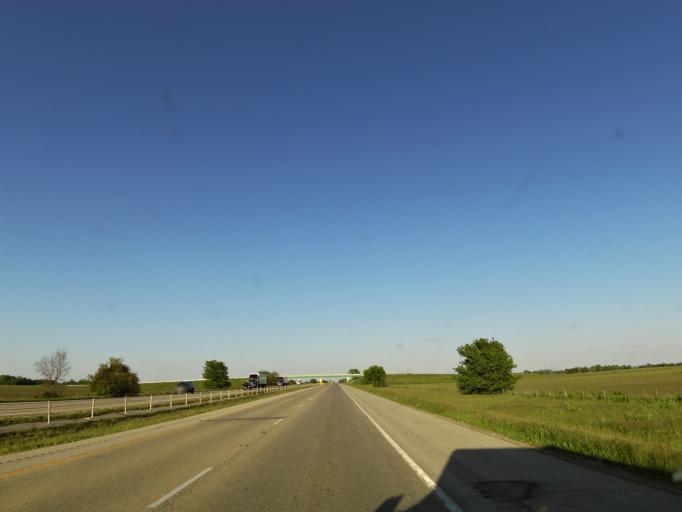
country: US
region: Illinois
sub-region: Champaign County
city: Urbana
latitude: 40.1204
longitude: -88.1294
